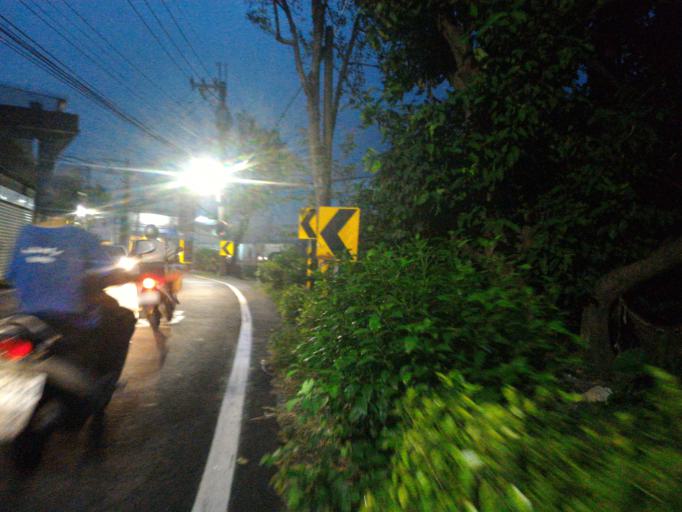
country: TW
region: Taiwan
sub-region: Taoyuan
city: Taoyuan
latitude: 24.9567
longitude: 121.3982
